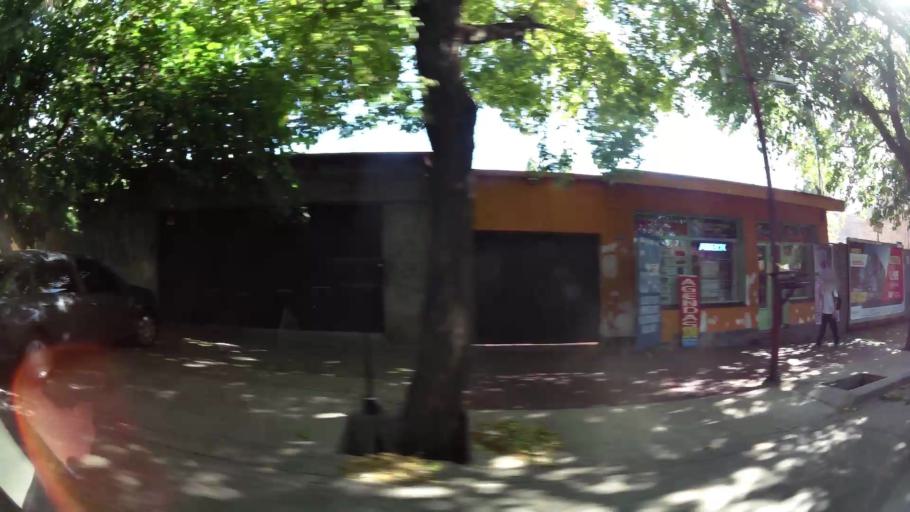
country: AR
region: Mendoza
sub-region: Departamento de Godoy Cruz
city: Godoy Cruz
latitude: -32.9238
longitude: -68.8563
